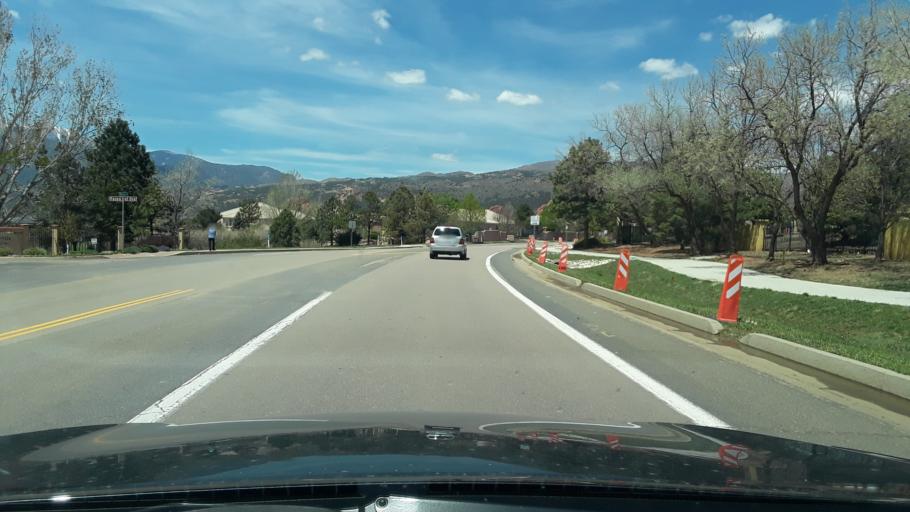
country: US
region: Colorado
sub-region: El Paso County
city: Colorado Springs
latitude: 38.8698
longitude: -104.8616
